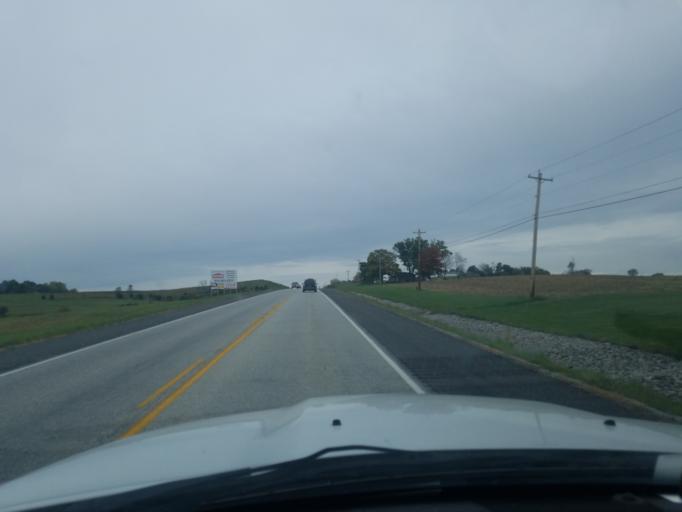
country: US
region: Indiana
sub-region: Washington County
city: Salem
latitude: 38.5756
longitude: -86.0980
